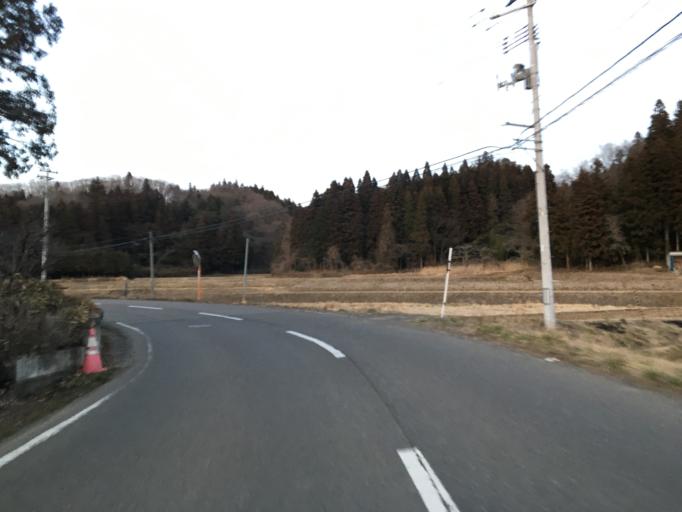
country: JP
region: Fukushima
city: Ishikawa
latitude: 37.0722
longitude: 140.3071
